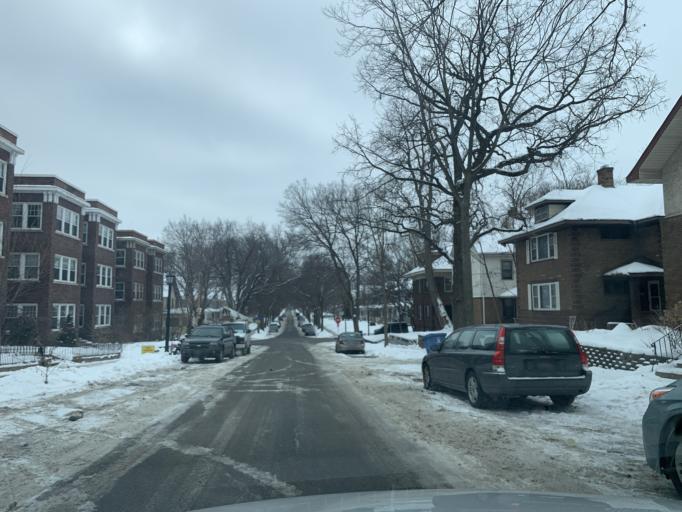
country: US
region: Minnesota
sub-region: Hennepin County
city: Minneapolis
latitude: 44.9634
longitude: -93.2957
